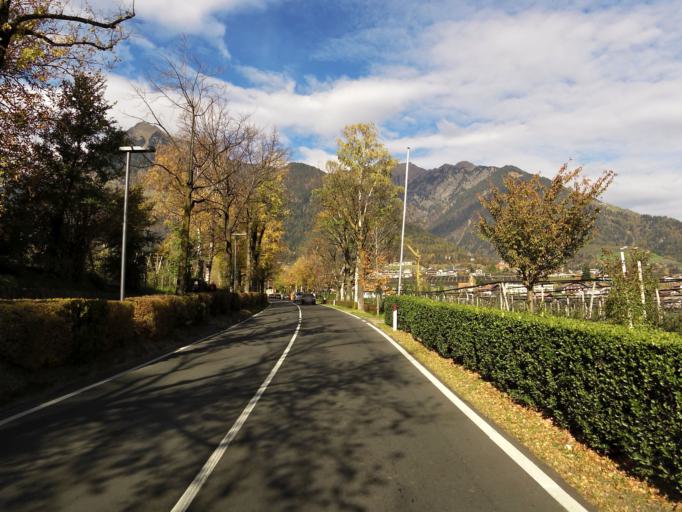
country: IT
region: Trentino-Alto Adige
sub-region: Bolzano
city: Tirolo
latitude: 46.6841
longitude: 11.1605
